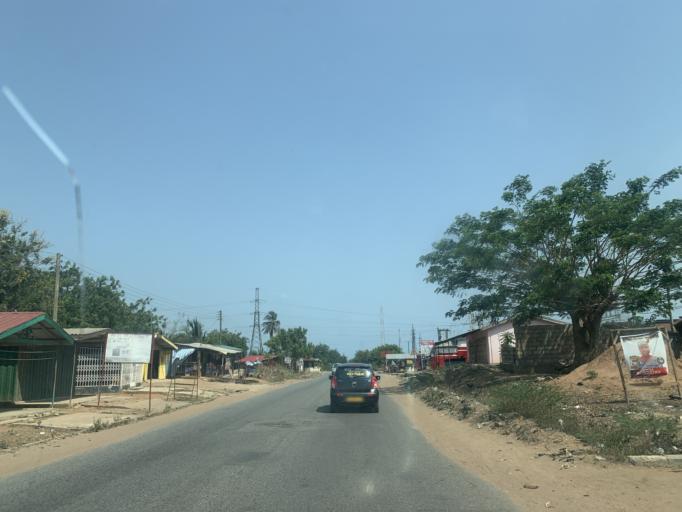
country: GH
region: Central
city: Winneba
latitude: 5.3903
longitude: -0.6459
